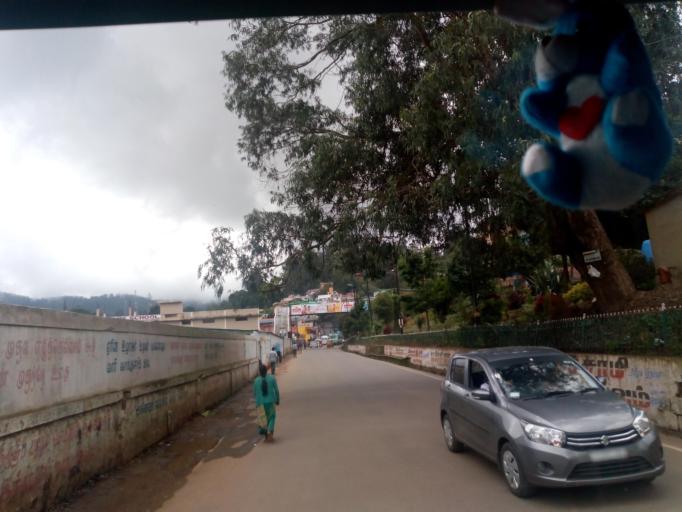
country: IN
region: Tamil Nadu
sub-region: Nilgiri
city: Ooty
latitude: 11.4058
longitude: 76.7045
